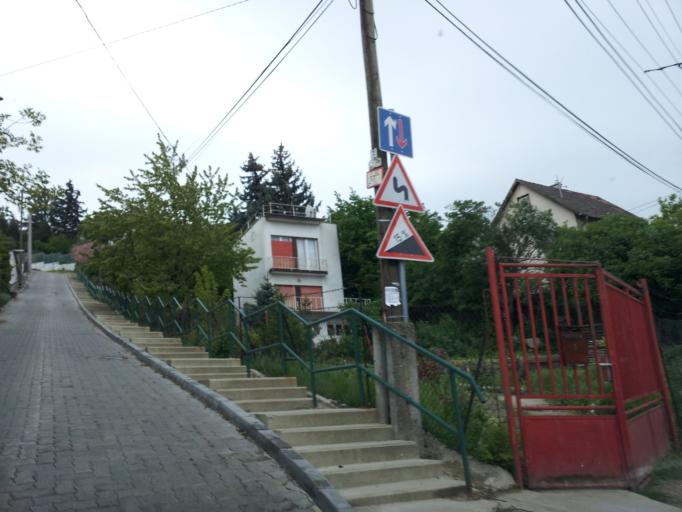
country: HU
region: Budapest
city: Budapest XXII. keruelet
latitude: 47.4391
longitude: 19.0209
